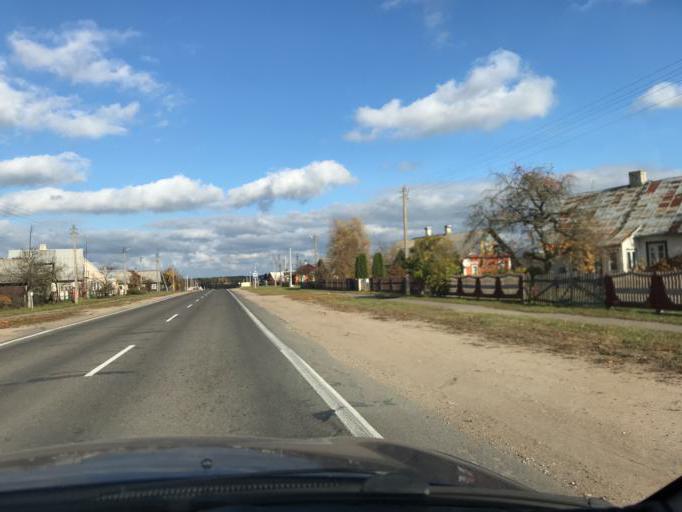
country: LT
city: Salcininkai
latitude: 54.2560
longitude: 25.3570
